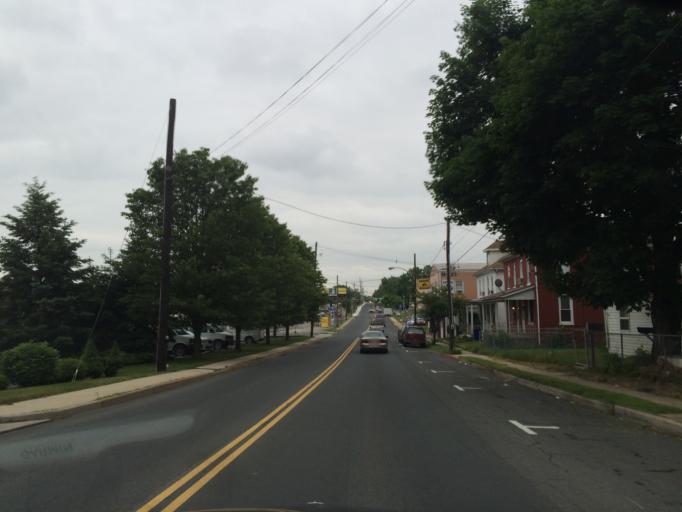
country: US
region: Maryland
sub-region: Washington County
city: Hagerstown
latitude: 39.6407
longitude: -77.7350
